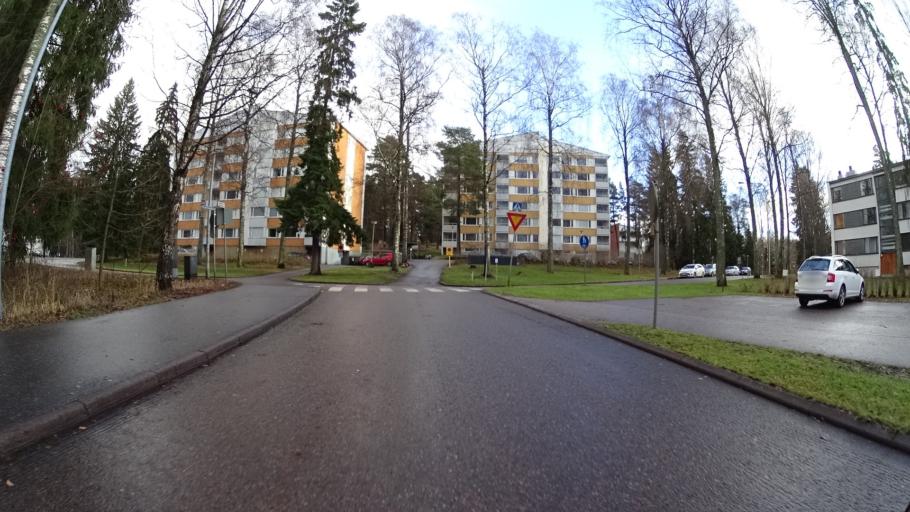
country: FI
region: Uusimaa
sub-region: Helsinki
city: Koukkuniemi
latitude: 60.1748
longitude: 24.7866
